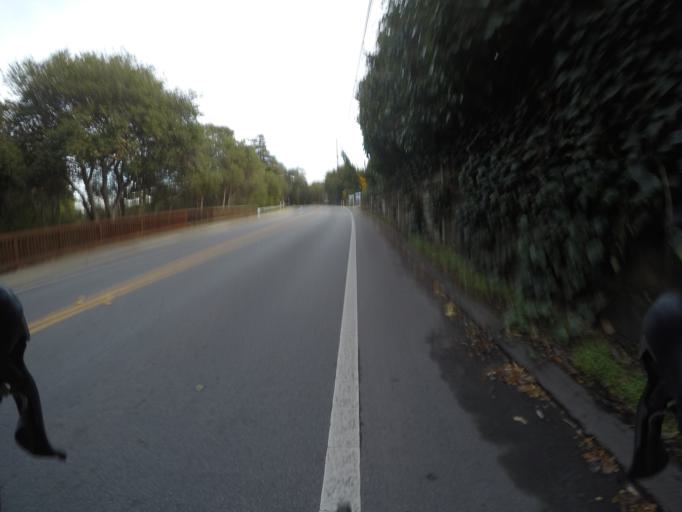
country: US
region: California
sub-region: Santa Cruz County
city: Capitola
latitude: 36.9804
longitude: -121.9591
